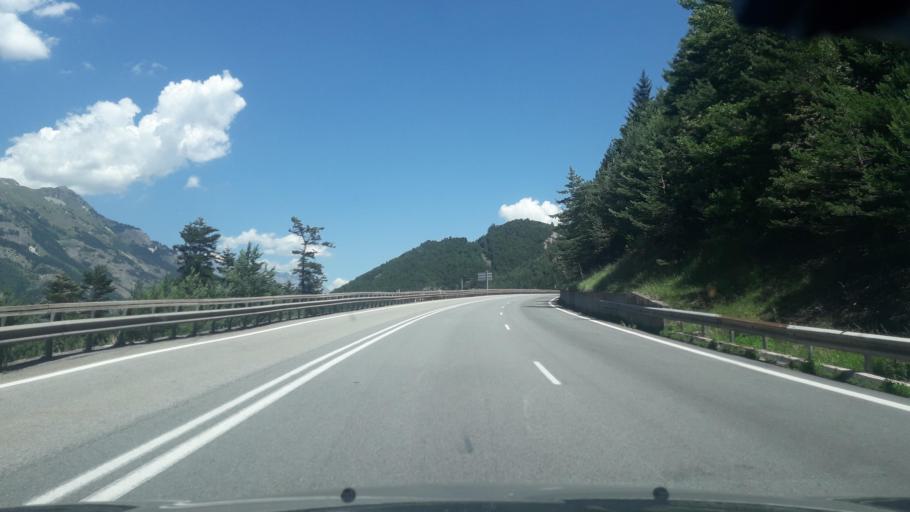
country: FR
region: Rhone-Alpes
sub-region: Departement de la Savoie
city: Modane
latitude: 45.1930
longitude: 6.6673
